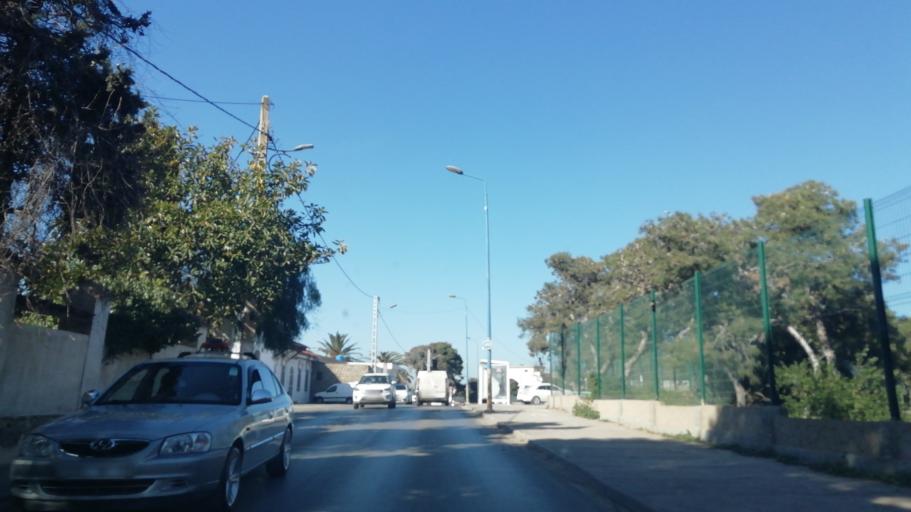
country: DZ
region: Oran
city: Bir el Djir
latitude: 35.7448
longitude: -0.5689
